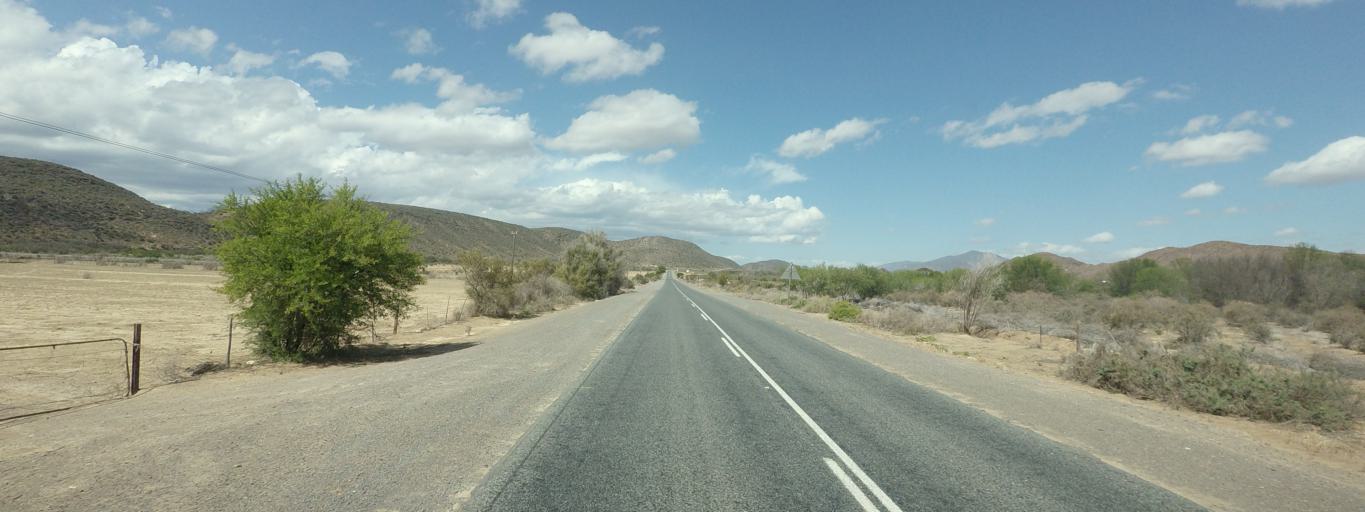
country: ZA
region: Western Cape
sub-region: Eden District Municipality
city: Ladismith
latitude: -33.5907
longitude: 21.1563
